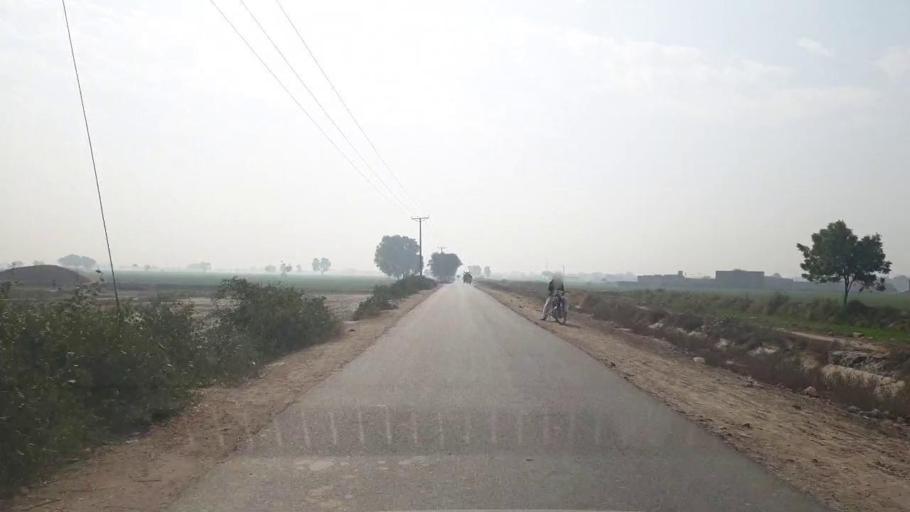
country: PK
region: Sindh
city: Hala
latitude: 25.8088
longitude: 68.4352
